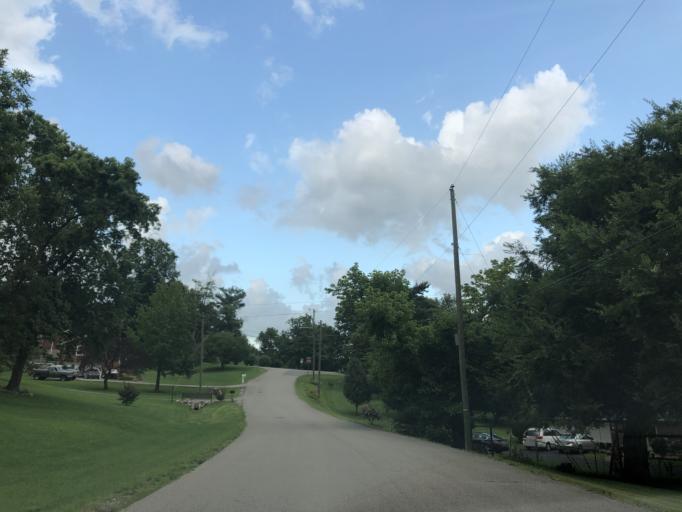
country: US
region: Tennessee
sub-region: Davidson County
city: Lakewood
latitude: 36.1759
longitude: -86.6902
